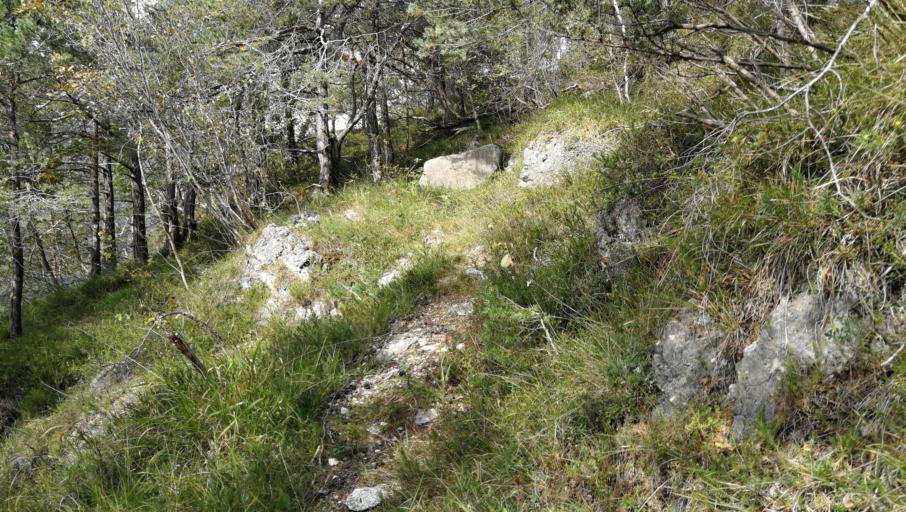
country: IT
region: Trentino-Alto Adige
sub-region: Provincia di Trento
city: Condino
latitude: 45.8848
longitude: 10.6054
